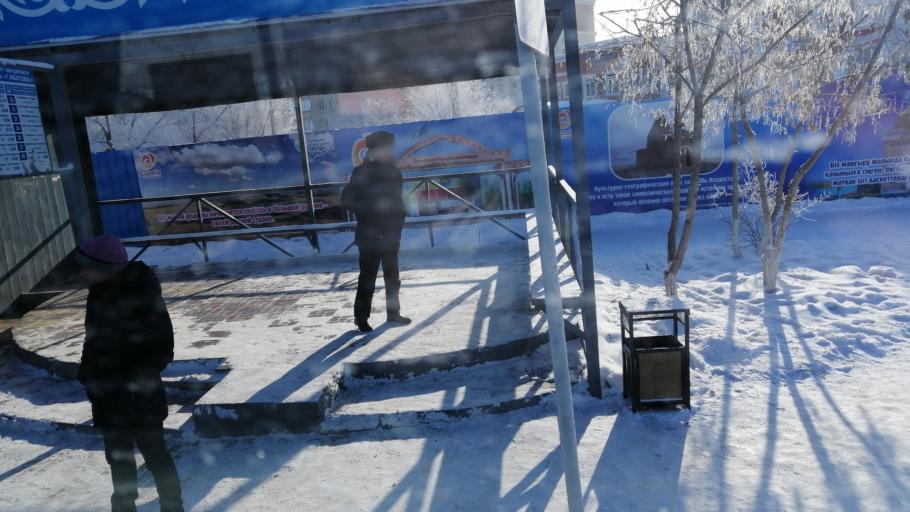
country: KZ
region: Aqtoebe
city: Aqtobe
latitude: 50.2912
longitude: 57.1657
